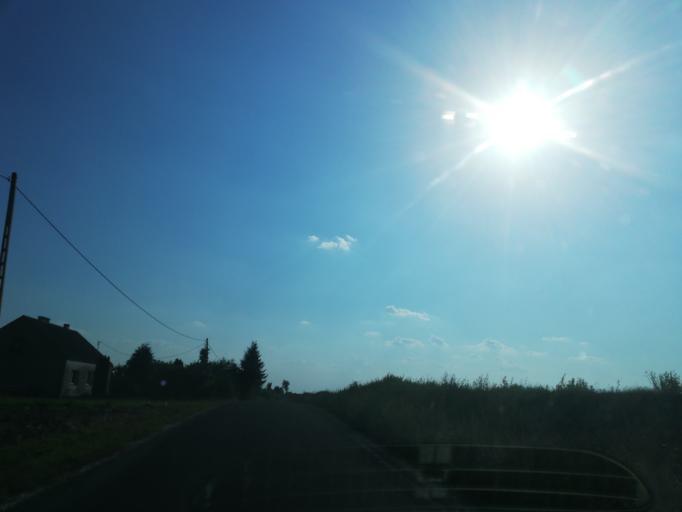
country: PL
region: Kujawsko-Pomorskie
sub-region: Powiat golubsko-dobrzynski
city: Kowalewo Pomorskie
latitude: 53.1094
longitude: 18.9043
